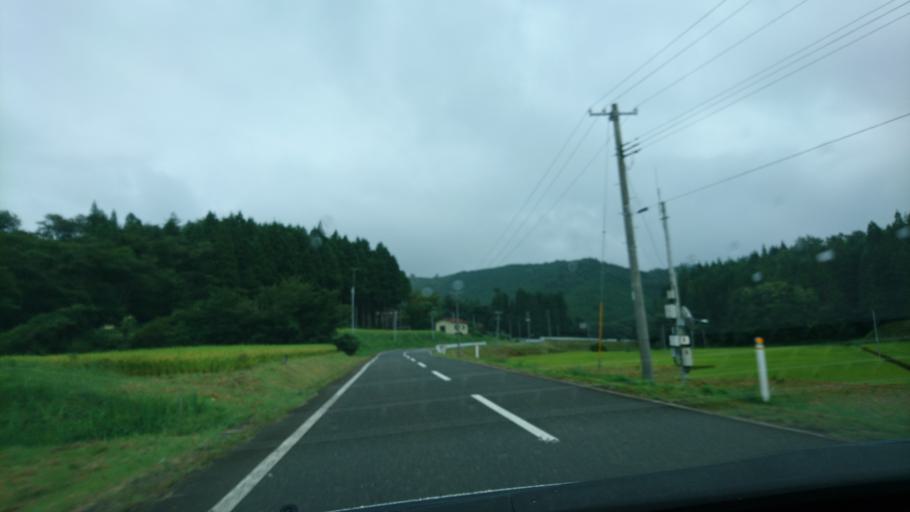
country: JP
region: Iwate
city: Ichinoseki
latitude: 38.8842
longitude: 140.9721
